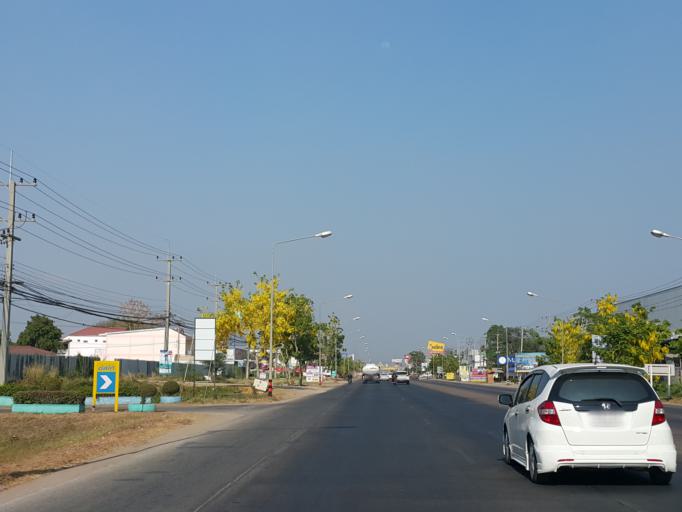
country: TH
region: Phitsanulok
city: Phitsanulok
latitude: 16.8165
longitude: 100.3077
